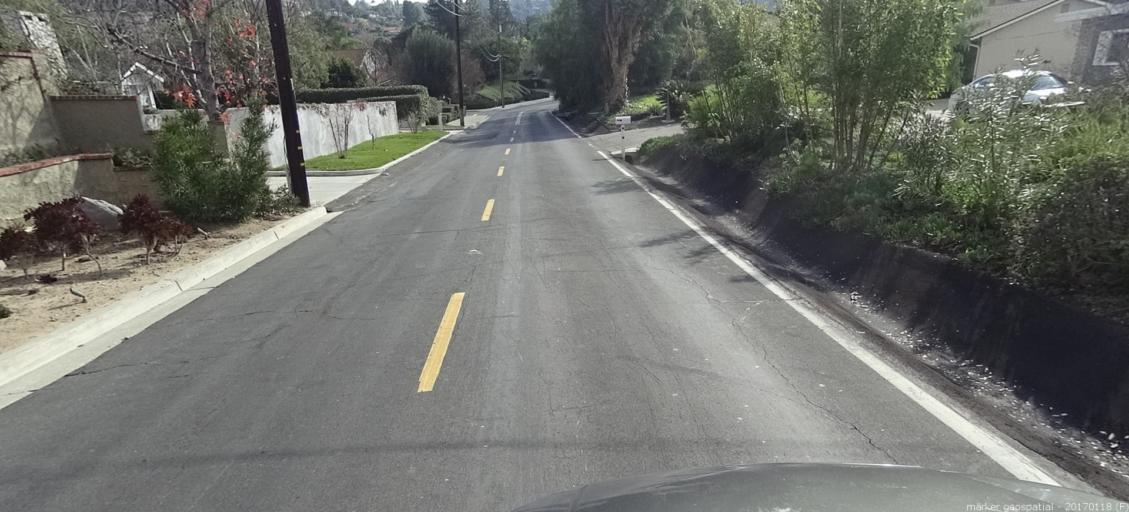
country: US
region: California
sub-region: Orange County
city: North Tustin
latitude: 33.7725
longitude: -117.7923
